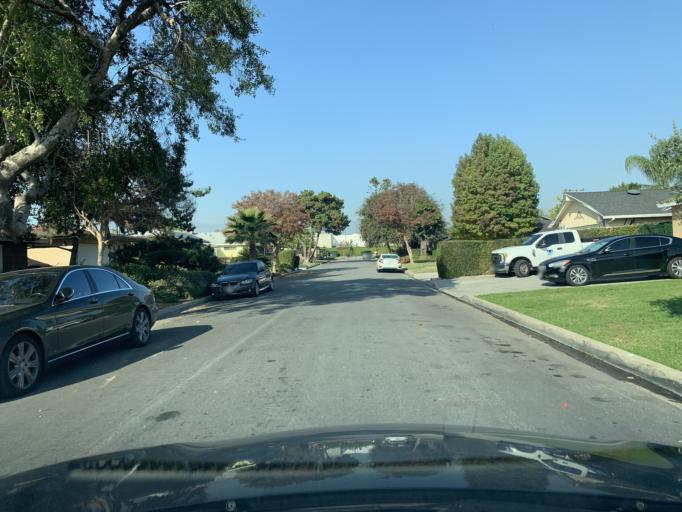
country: US
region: California
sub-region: Los Angeles County
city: Covina
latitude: 34.0763
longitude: -117.8971
